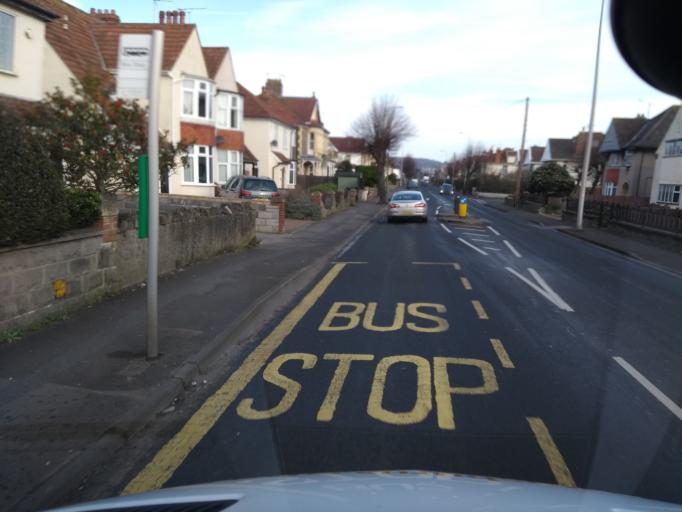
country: GB
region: England
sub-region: North Somerset
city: Weston-super-Mare
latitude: 51.3315
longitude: -2.9735
